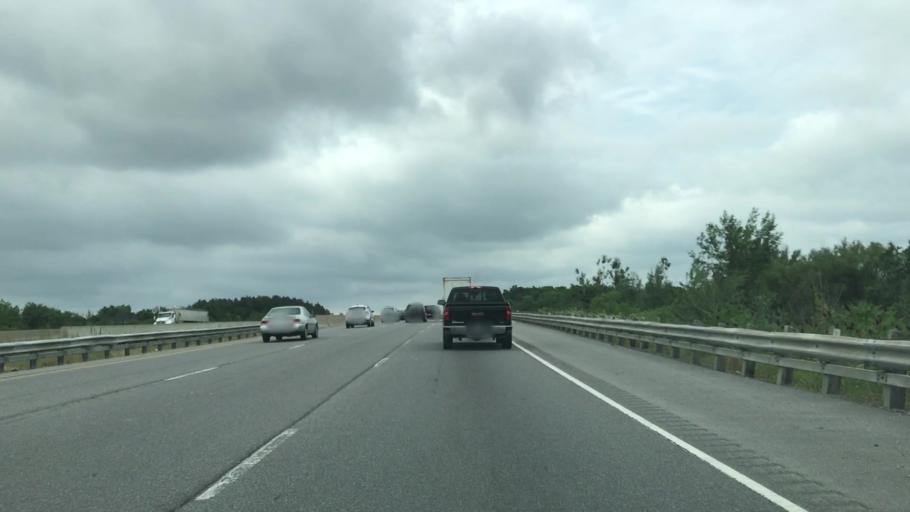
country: CA
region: Ontario
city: Newmarket
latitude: 43.9938
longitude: -79.3961
